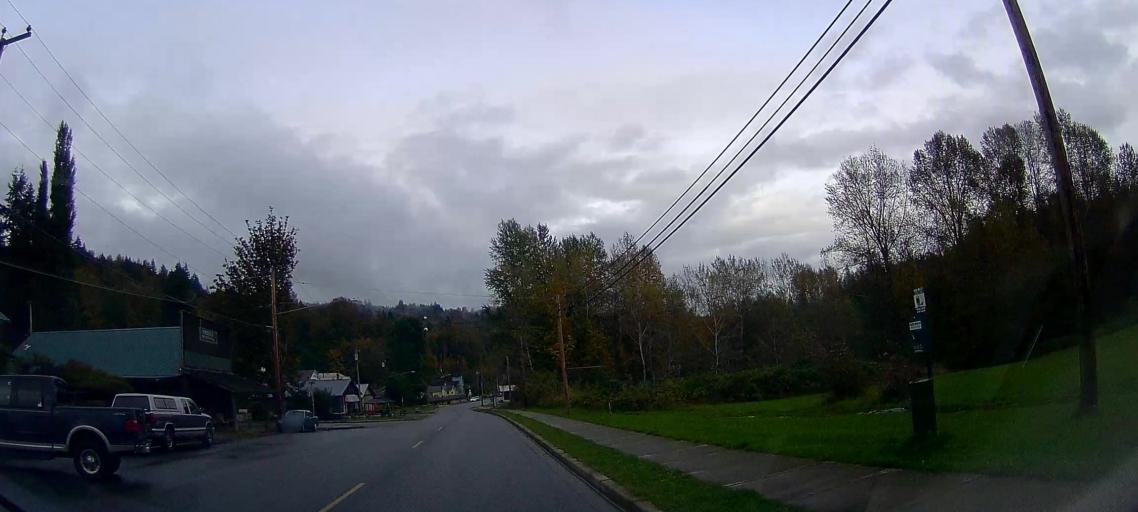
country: US
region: Washington
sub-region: Snohomish County
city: Darrington
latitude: 48.5385
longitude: -121.7543
